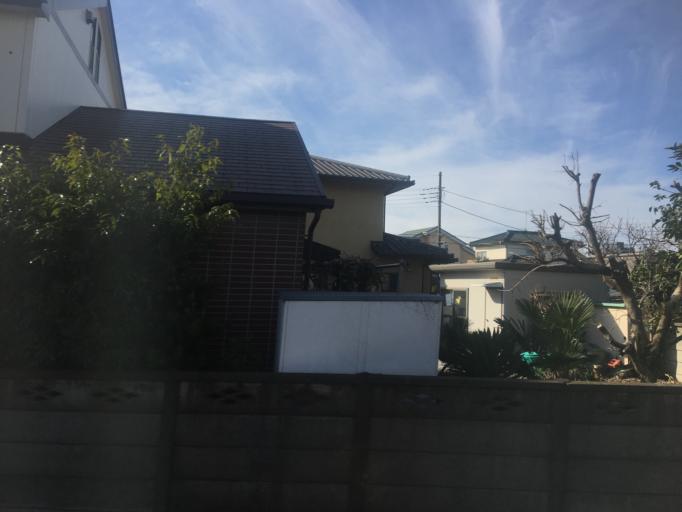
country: JP
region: Saitama
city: Kawagoe
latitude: 35.9261
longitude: 139.4416
